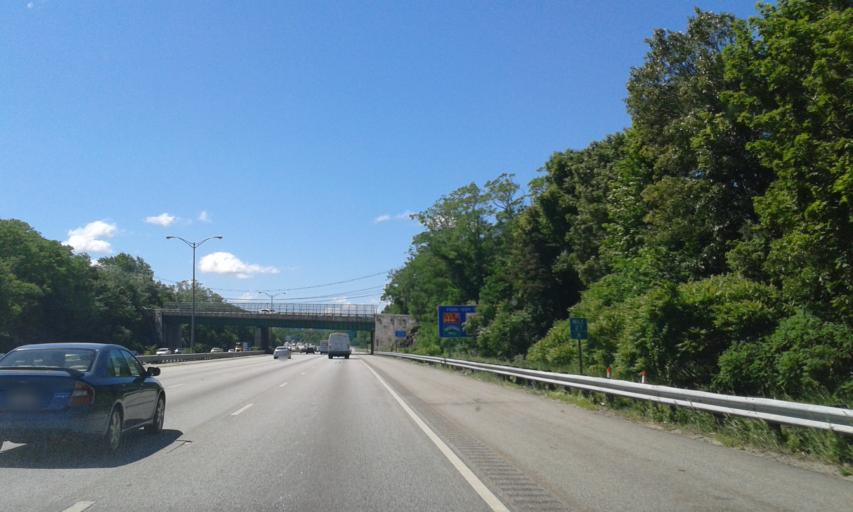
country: US
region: Massachusetts
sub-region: Middlesex County
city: Stoneham
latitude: 42.4926
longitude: -71.1181
